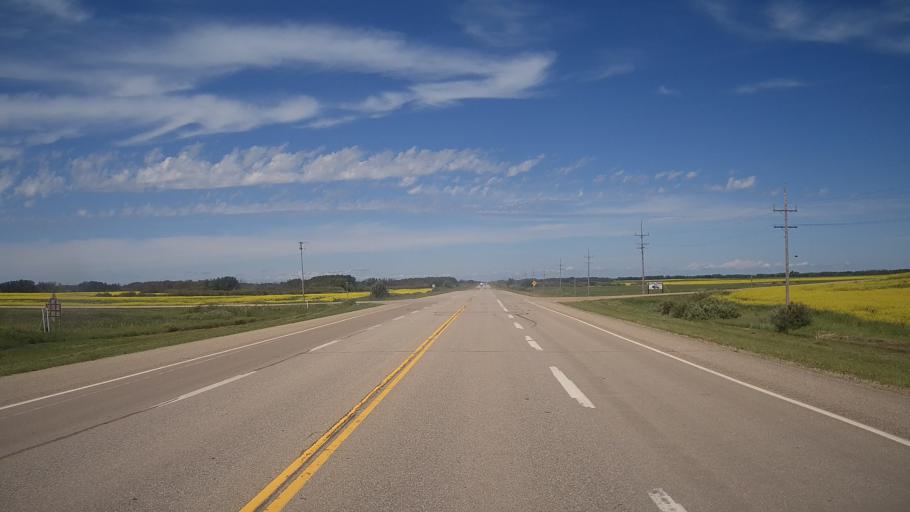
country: CA
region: Saskatchewan
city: Langenburg
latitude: 50.6373
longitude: -101.2759
